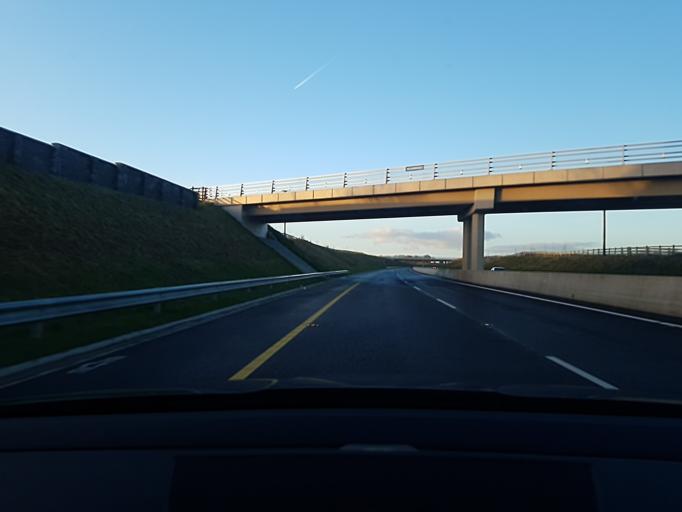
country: IE
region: Connaught
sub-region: County Galway
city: Tuam
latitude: 53.4355
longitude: -8.8450
